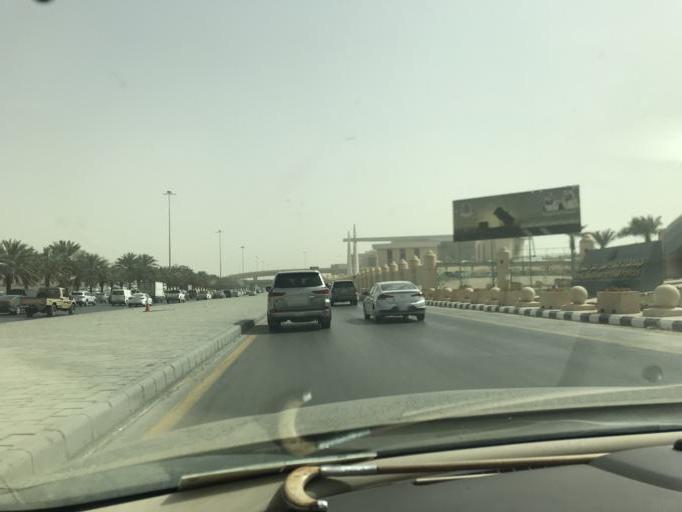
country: SA
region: Ar Riyad
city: Riyadh
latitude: 24.7437
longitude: 46.7466
